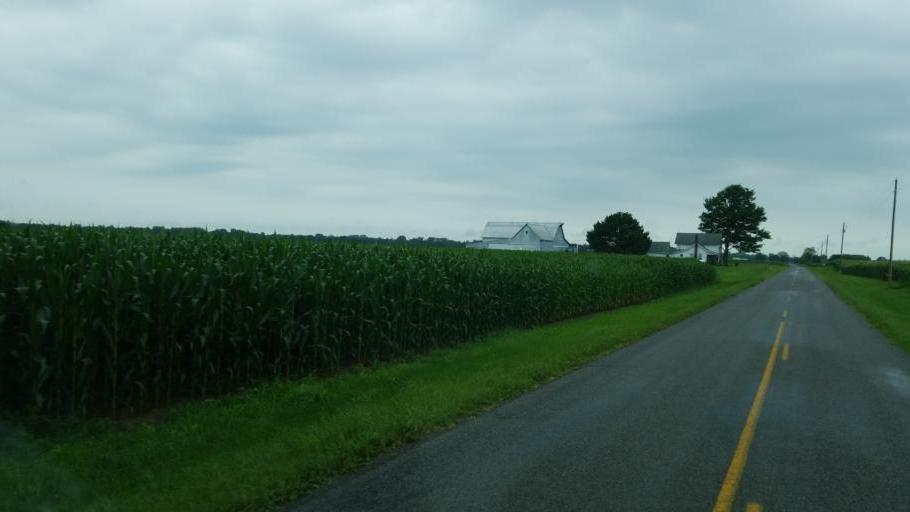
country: US
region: Ohio
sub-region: Union County
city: Richwood
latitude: 40.5126
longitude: -83.4591
